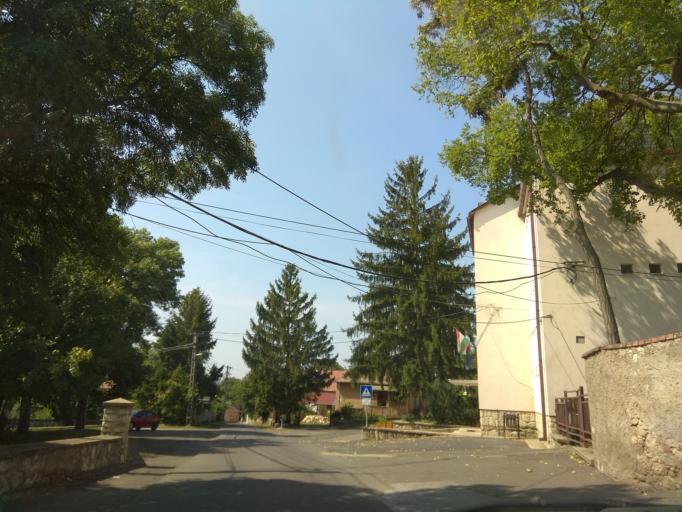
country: HU
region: Borsod-Abauj-Zemplen
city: Tallya
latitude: 48.2331
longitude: 21.2339
